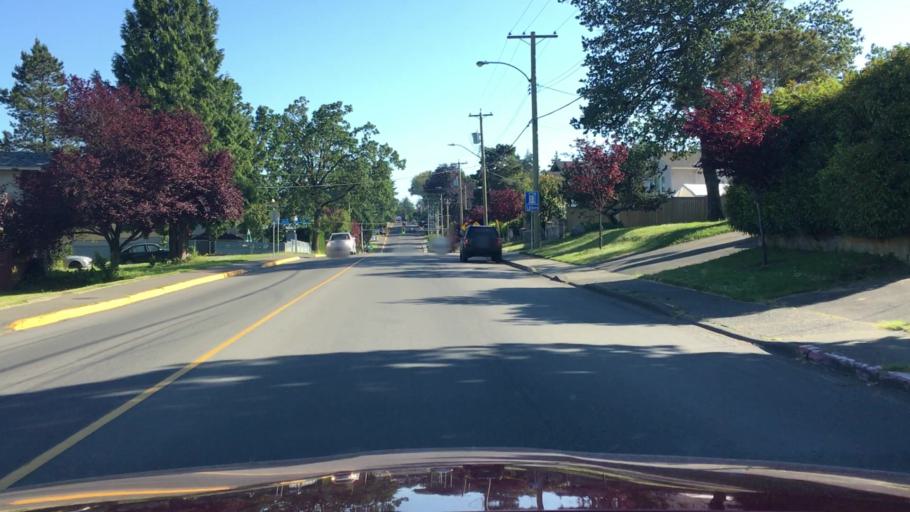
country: CA
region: British Columbia
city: Victoria
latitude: 48.4386
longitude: -123.4020
